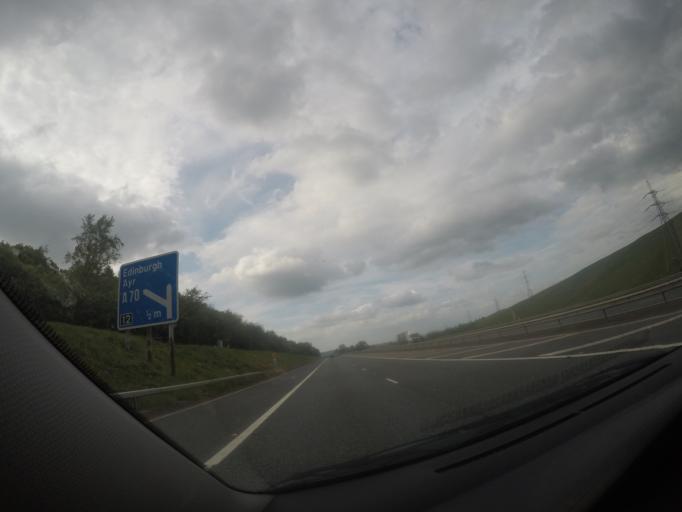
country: GB
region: Scotland
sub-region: South Lanarkshire
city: Douglas
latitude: 55.5618
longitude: -3.8045
